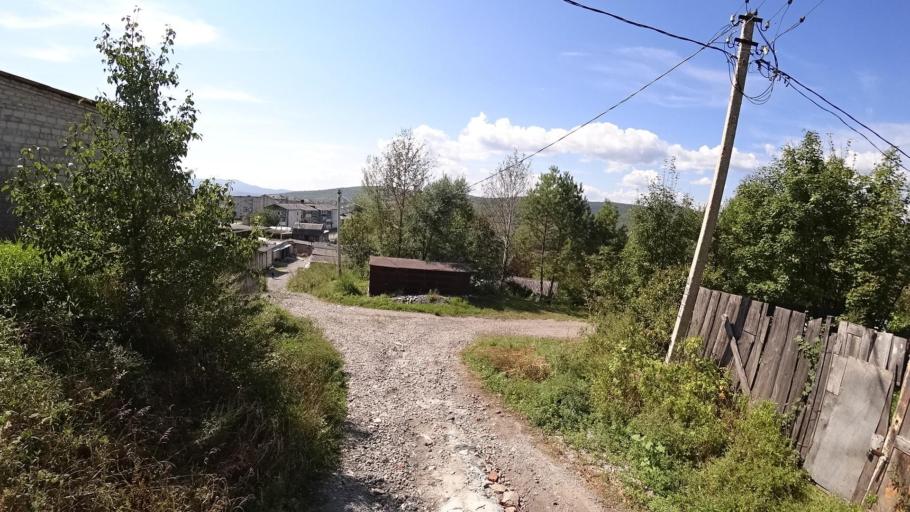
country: RU
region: Jewish Autonomous Oblast
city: Londoko
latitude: 49.0173
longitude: 131.8854
